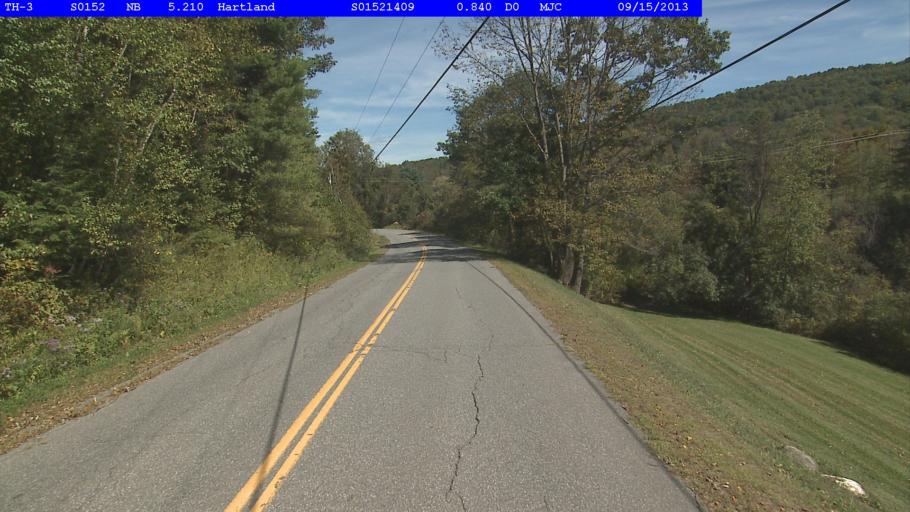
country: US
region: Vermont
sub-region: Windsor County
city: Windsor
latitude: 43.5337
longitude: -72.4356
